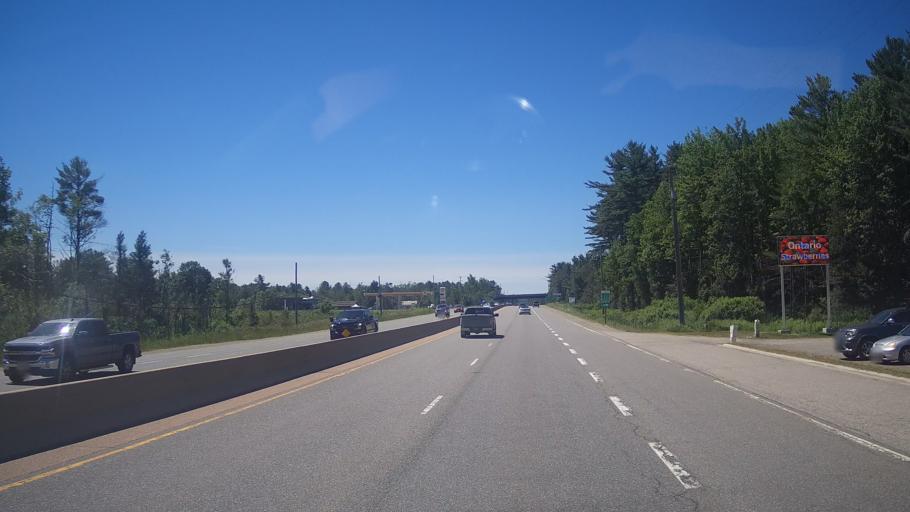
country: CA
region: Ontario
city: Gravenhurst
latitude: 44.8480
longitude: -79.3164
